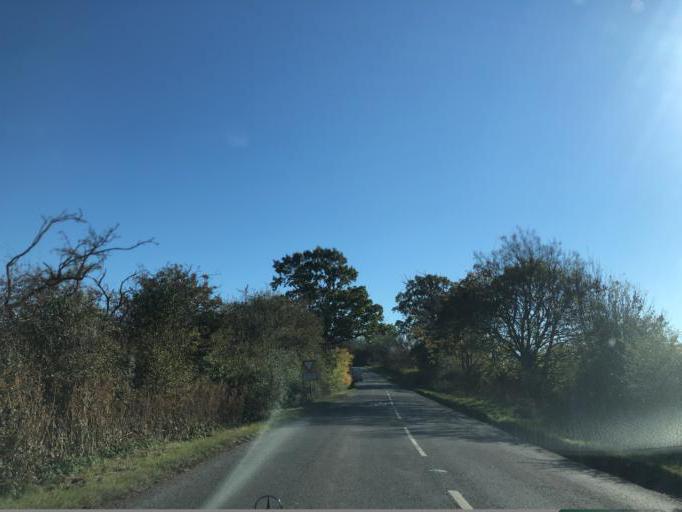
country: GB
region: England
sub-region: Warwickshire
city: Harbury
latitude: 52.2416
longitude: -1.4993
